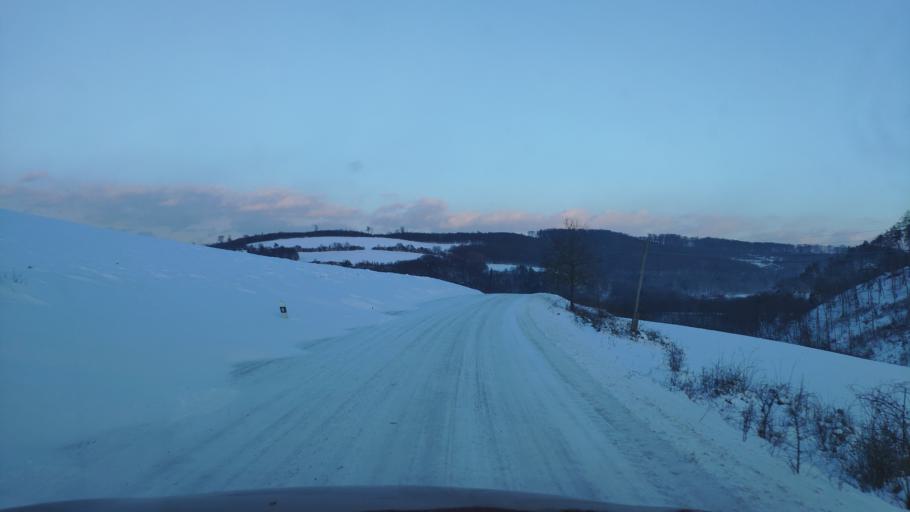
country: SK
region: Presovsky
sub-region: Okres Presov
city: Presov
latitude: 48.9125
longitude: 21.1927
